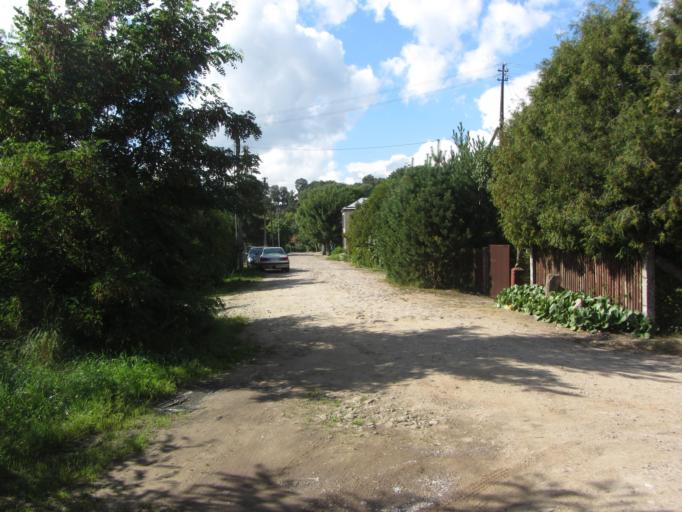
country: LT
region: Kauno apskritis
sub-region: Kauno rajonas
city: Akademija (Kaunas)
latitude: 54.9341
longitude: 23.7910
